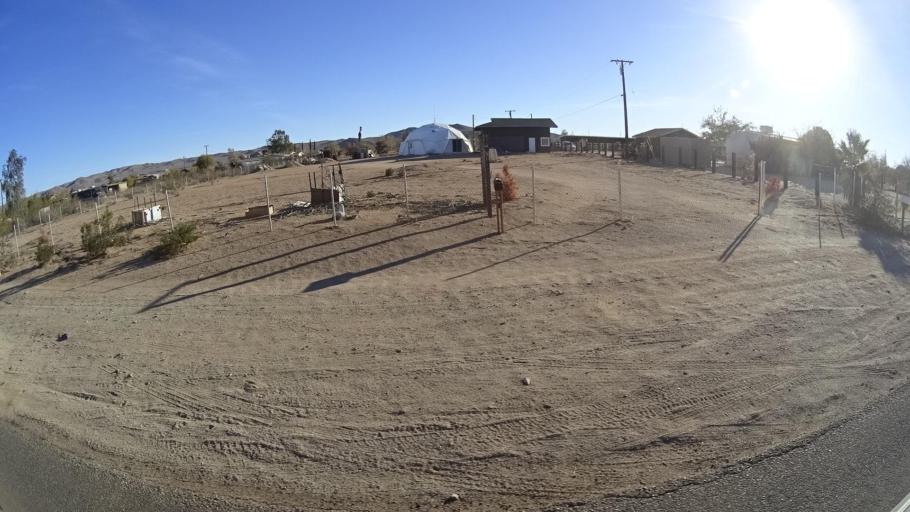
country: US
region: California
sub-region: Kern County
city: Ridgecrest
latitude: 35.6007
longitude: -117.7020
